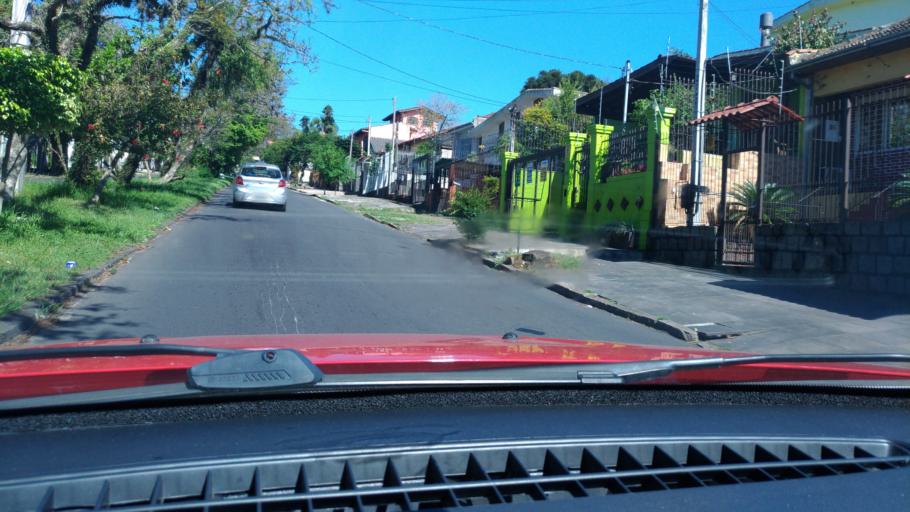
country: BR
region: Rio Grande do Sul
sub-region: Porto Alegre
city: Porto Alegre
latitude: -30.0299
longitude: -51.1456
